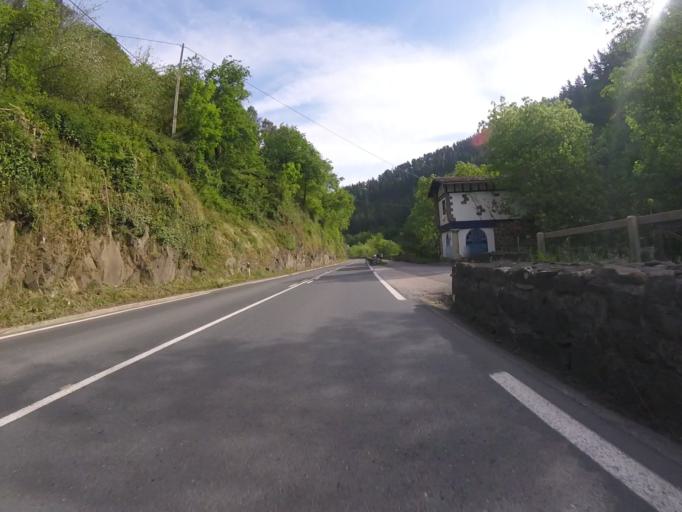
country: ES
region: Basque Country
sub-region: Provincia de Guipuzcoa
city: Urretxu
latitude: 43.1020
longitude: -2.3177
